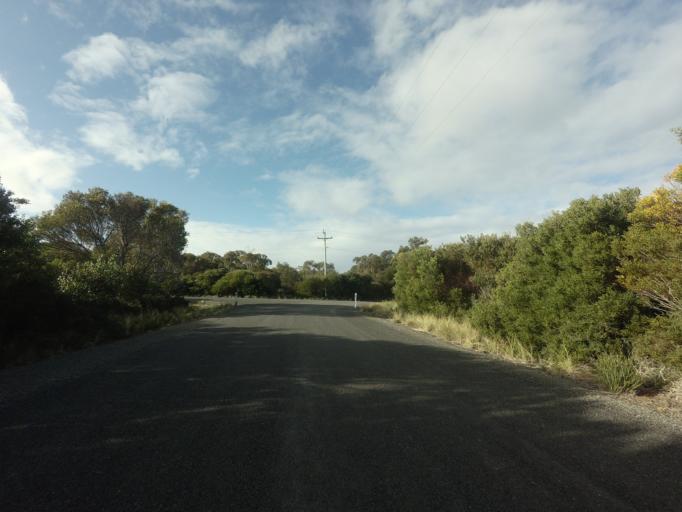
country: AU
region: Tasmania
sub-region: Break O'Day
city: St Helens
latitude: -42.0953
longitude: 148.2315
